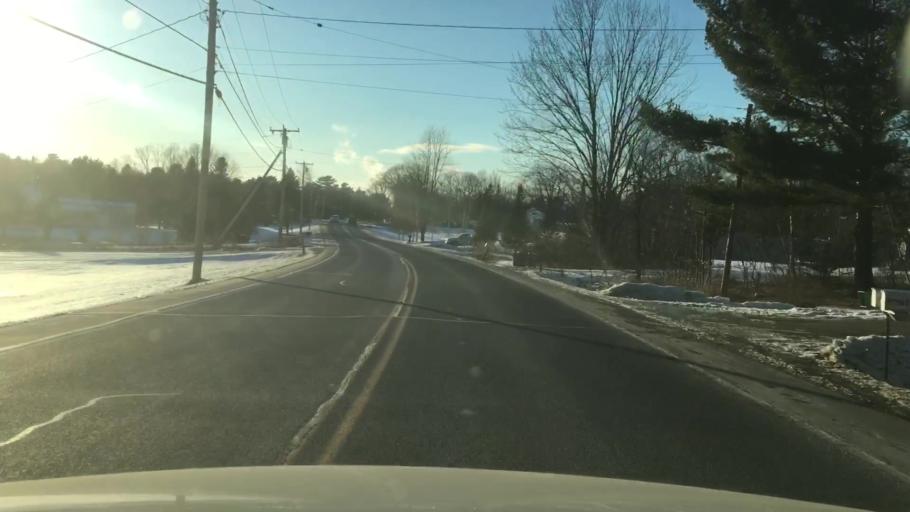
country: US
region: Maine
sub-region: Penobscot County
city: Eddington
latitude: 44.8297
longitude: -68.6721
